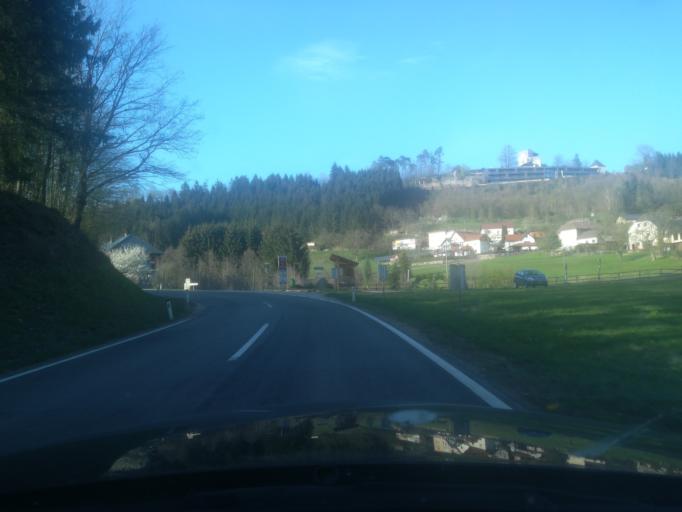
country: AT
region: Upper Austria
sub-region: Politischer Bezirk Perg
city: Bad Kreuzen
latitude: 48.2564
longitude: 14.8166
